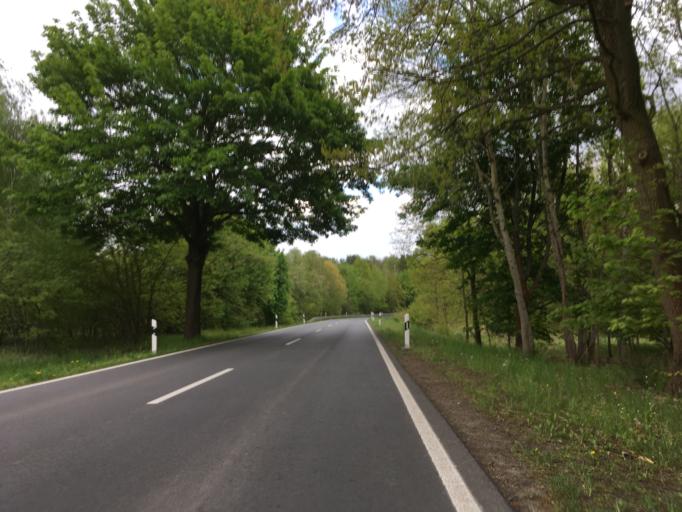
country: DE
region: Brandenburg
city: Bernau bei Berlin
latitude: 52.6449
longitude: 13.6092
